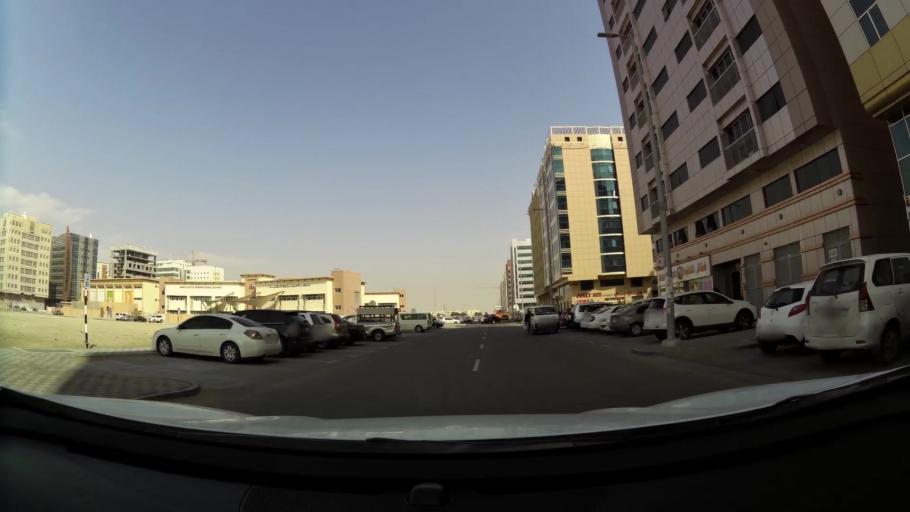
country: AE
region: Abu Dhabi
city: Abu Dhabi
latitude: 24.3416
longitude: 54.5319
